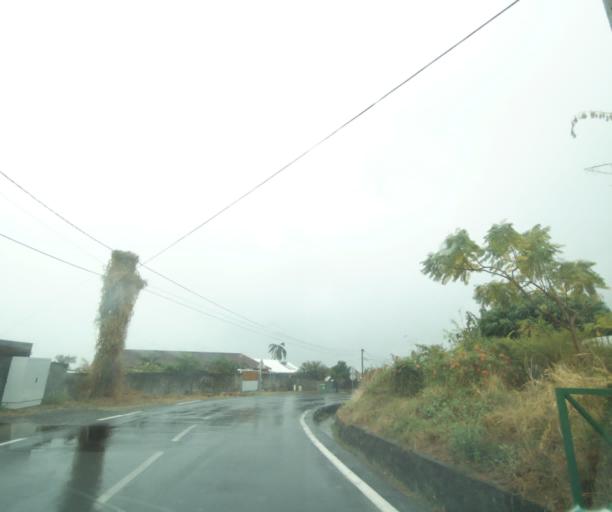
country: RE
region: Reunion
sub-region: Reunion
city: La Possession
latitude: -20.9793
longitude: 55.3284
